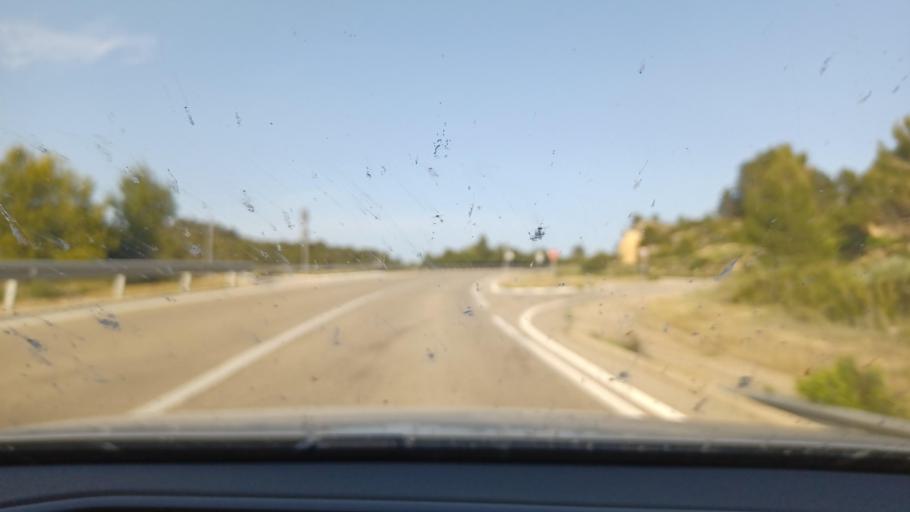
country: ES
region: Catalonia
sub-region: Provincia de Tarragona
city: Batea
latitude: 41.1046
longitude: 0.2819
